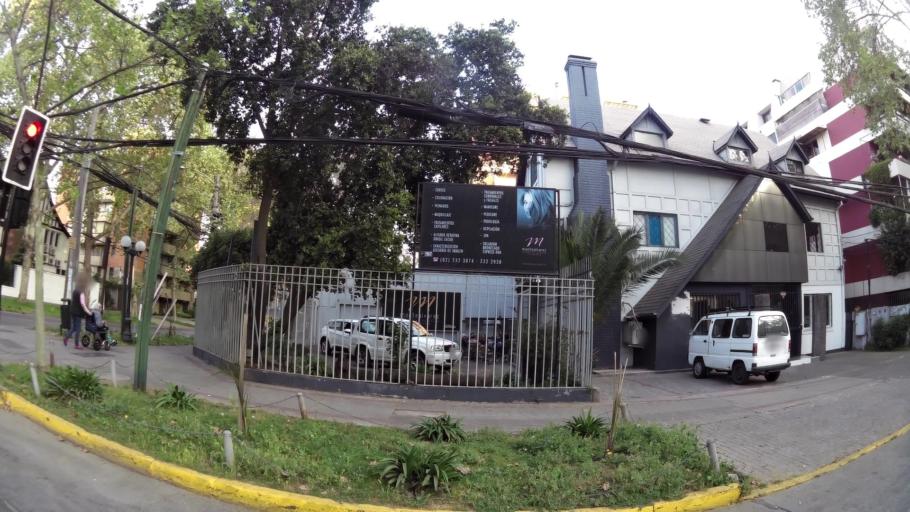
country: CL
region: Santiago Metropolitan
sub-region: Provincia de Santiago
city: Villa Presidente Frei, Nunoa, Santiago, Chile
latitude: -33.4239
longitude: -70.6069
